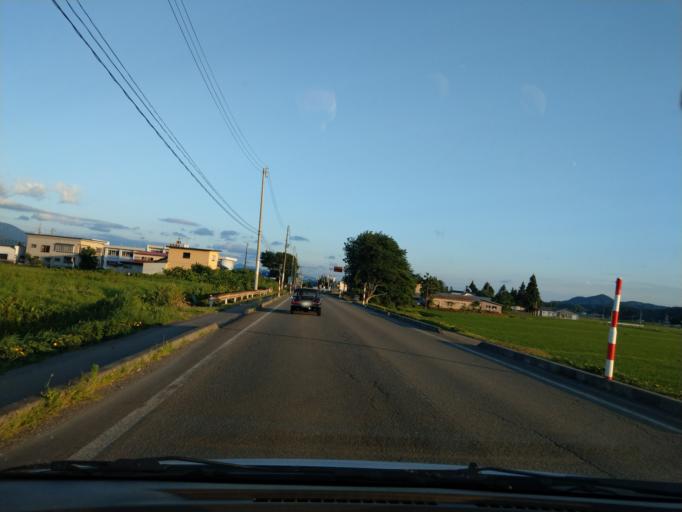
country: JP
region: Akita
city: Kakunodatemachi
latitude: 39.6578
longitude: 140.5703
